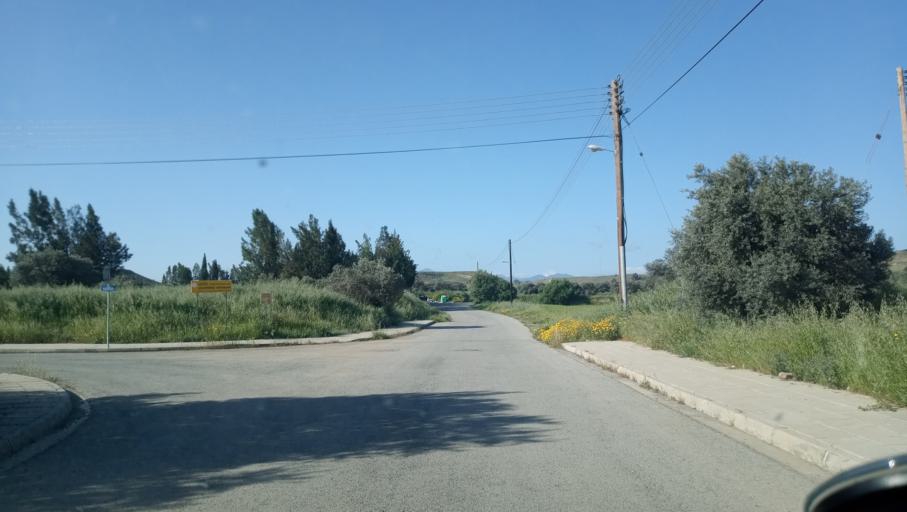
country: CY
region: Lefkosia
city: Tseri
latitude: 35.0672
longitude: 33.3160
